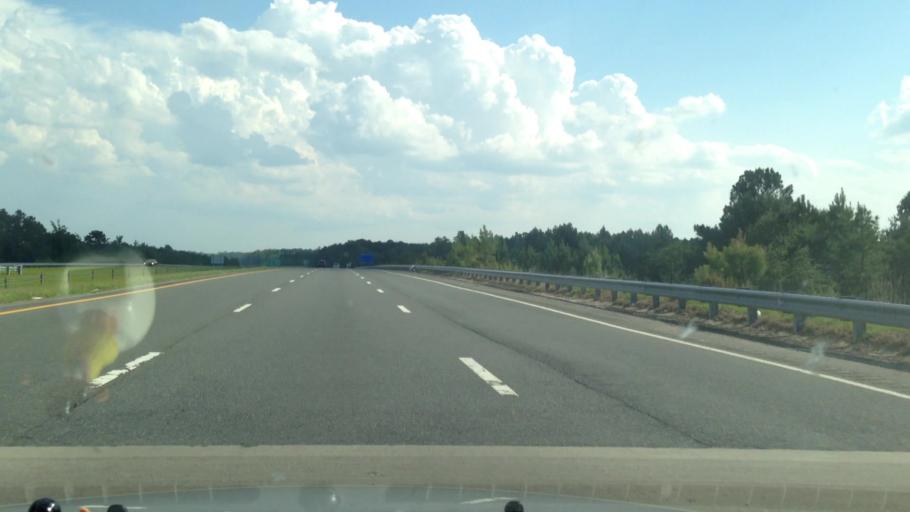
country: US
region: North Carolina
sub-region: Lee County
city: Broadway
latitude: 35.4602
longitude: -79.1182
